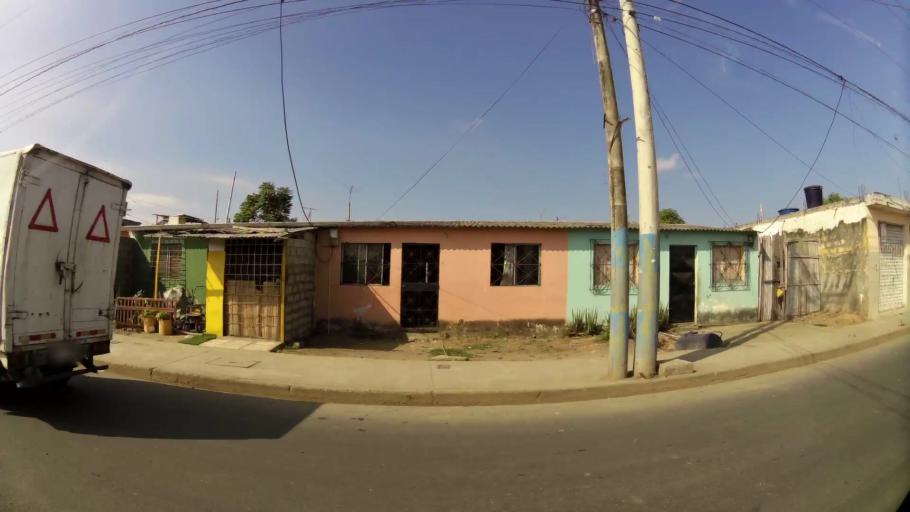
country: EC
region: Guayas
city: Eloy Alfaro
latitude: -2.1658
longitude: -79.7972
